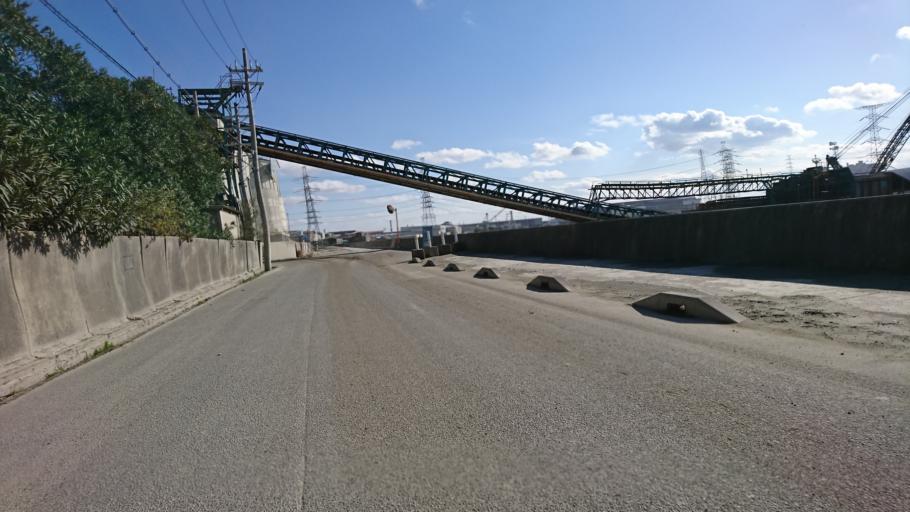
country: JP
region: Hyogo
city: Shirahamacho-usazakiminami
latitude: 34.7618
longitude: 134.7624
